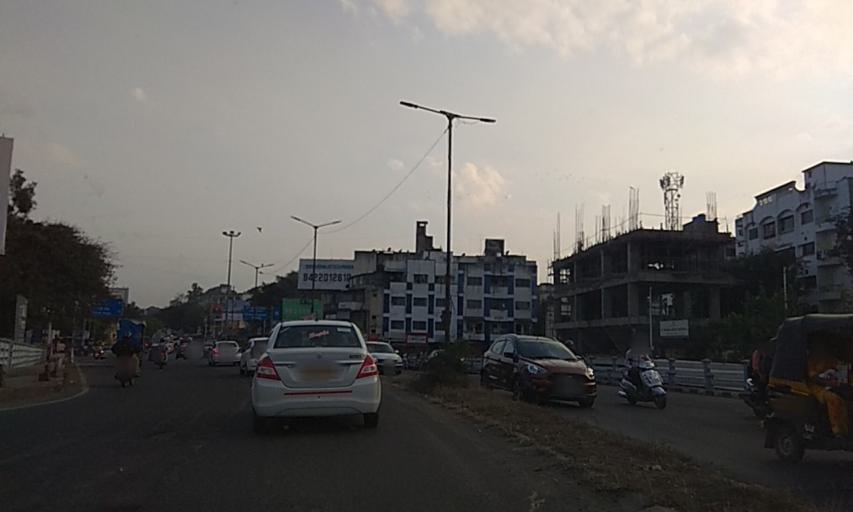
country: IN
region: Maharashtra
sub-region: Pune Division
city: Khadki
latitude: 18.5674
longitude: 73.8116
